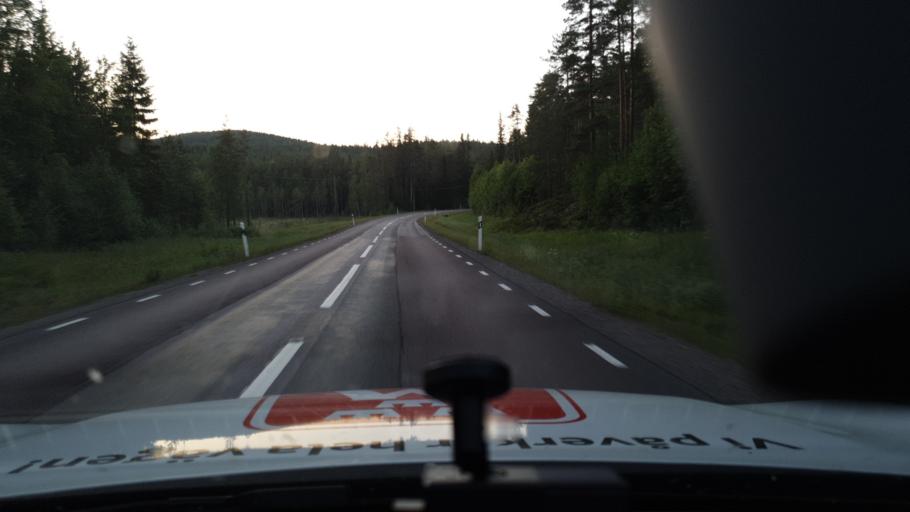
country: SE
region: Vaermland
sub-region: Torsby Kommun
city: Torsby
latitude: 60.3085
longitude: 13.0952
